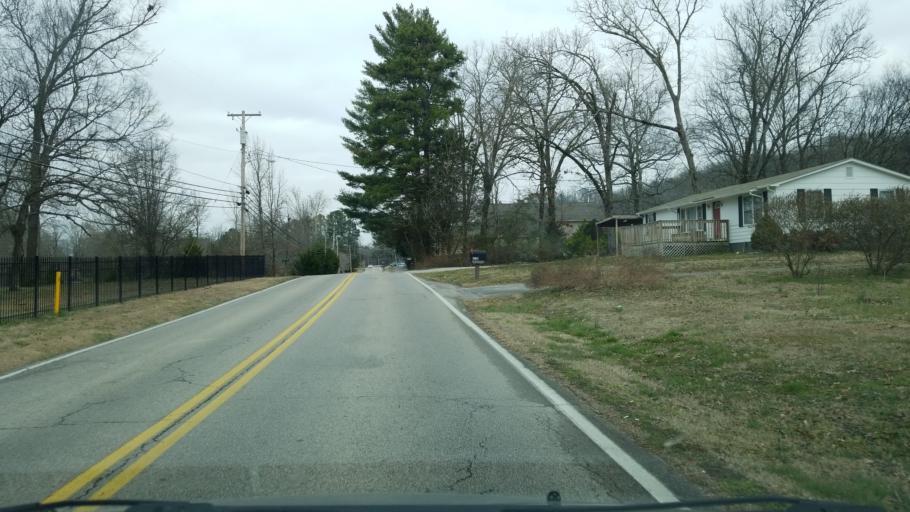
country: US
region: Tennessee
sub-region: Hamilton County
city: East Brainerd
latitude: 35.0113
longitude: -85.1274
